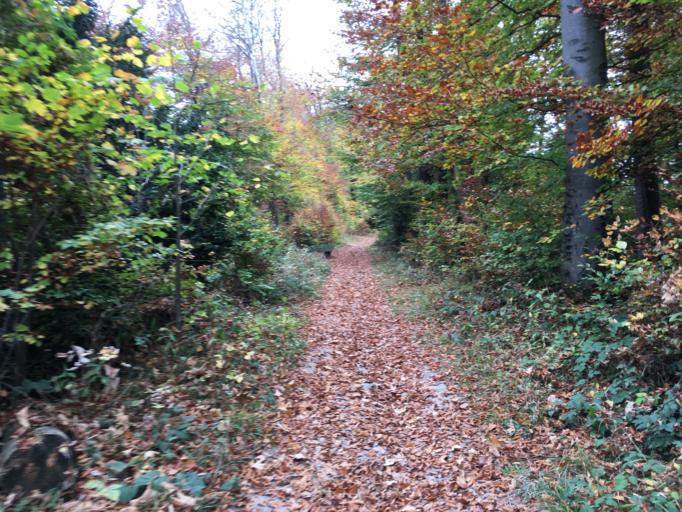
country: CH
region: Zurich
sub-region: Bezirk Horgen
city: Adliswil / Oberleimbach
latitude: 47.3190
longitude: 8.5038
